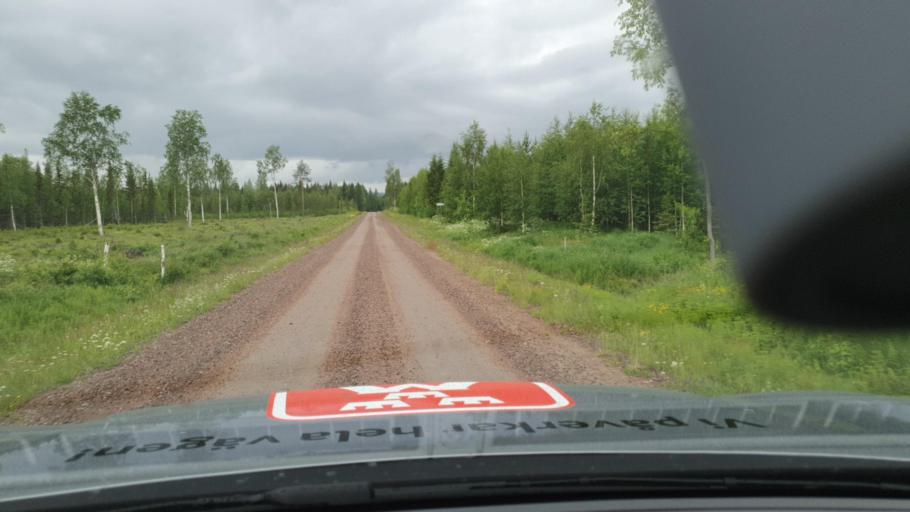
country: SE
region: Norrbotten
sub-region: Overkalix Kommun
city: OEverkalix
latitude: 66.6103
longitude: 22.7410
